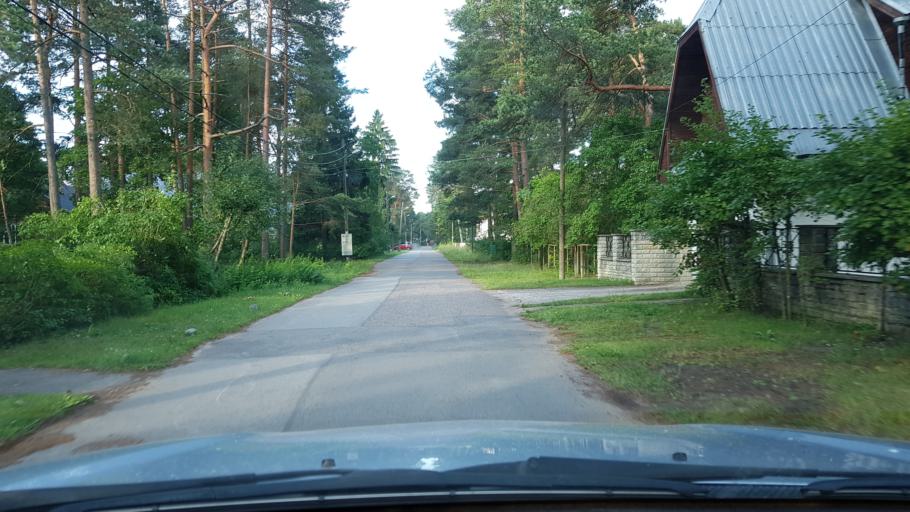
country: EE
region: Ida-Virumaa
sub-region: Narva-Joesuu linn
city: Narva-Joesuu
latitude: 59.4556
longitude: 28.0560
